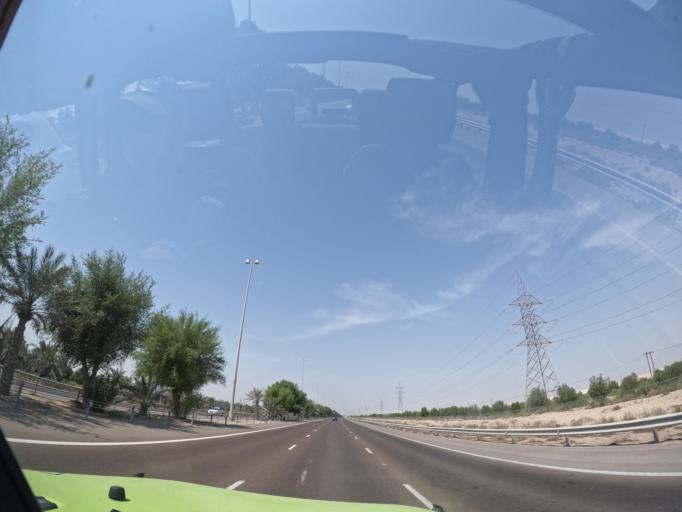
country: AE
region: Abu Dhabi
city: Abu Dhabi
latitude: 24.2235
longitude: 54.8110
